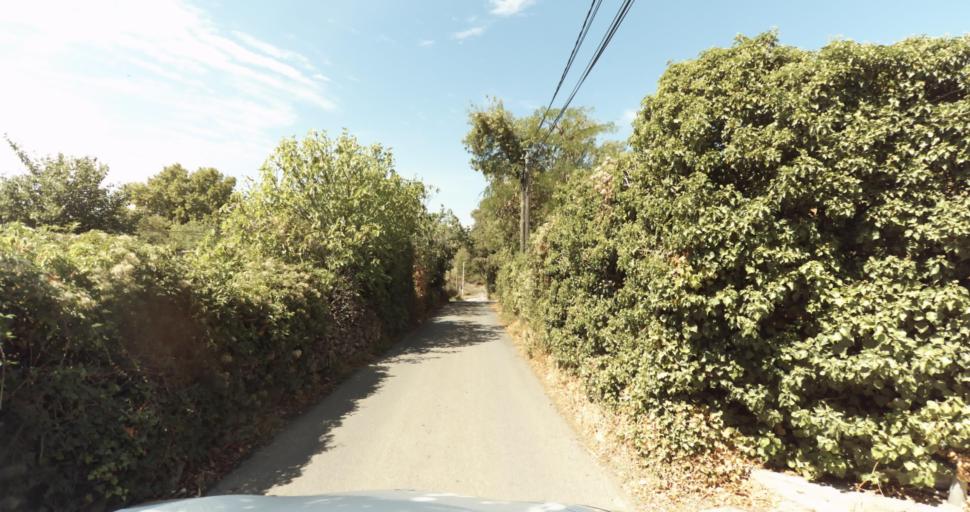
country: FR
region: Provence-Alpes-Cote d'Azur
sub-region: Departement des Bouches-du-Rhone
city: Miramas
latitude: 43.5782
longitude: 5.0161
